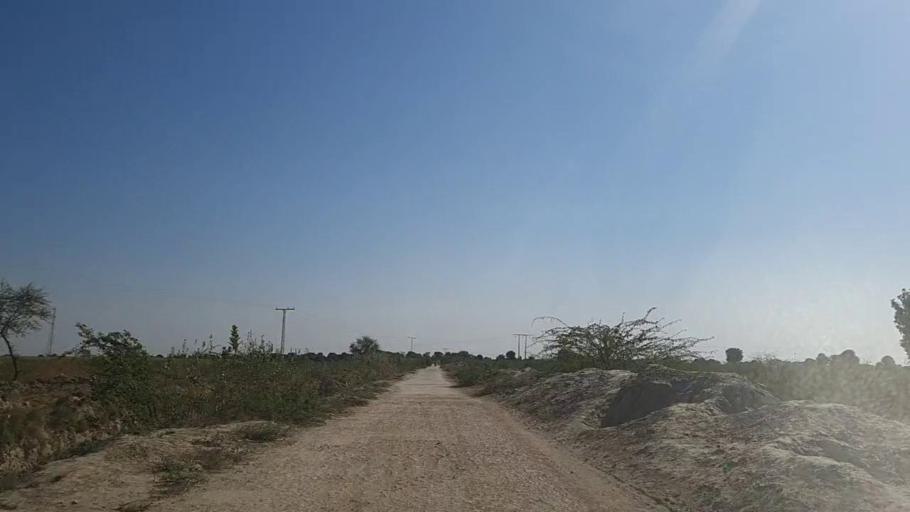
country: PK
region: Sindh
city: Samaro
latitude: 25.2352
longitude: 69.4841
